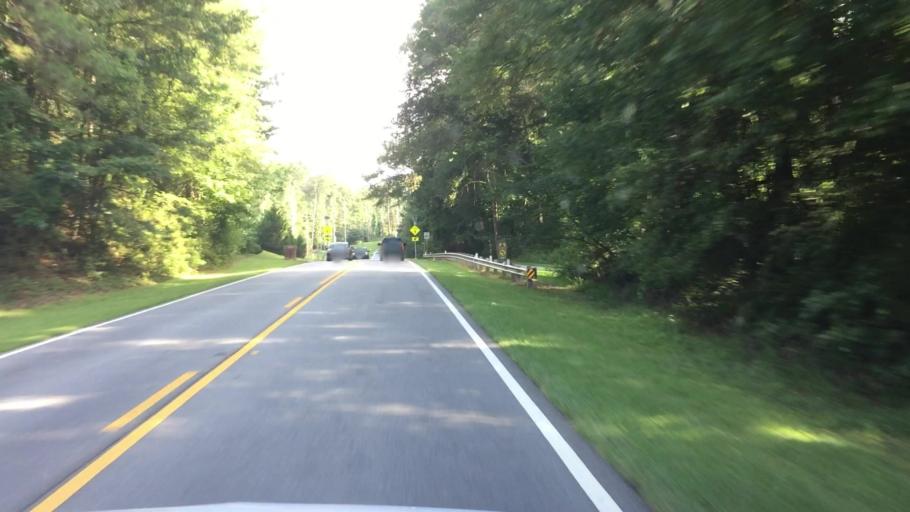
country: US
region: Georgia
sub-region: DeKalb County
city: Pine Mountain
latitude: 33.6257
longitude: -84.1302
